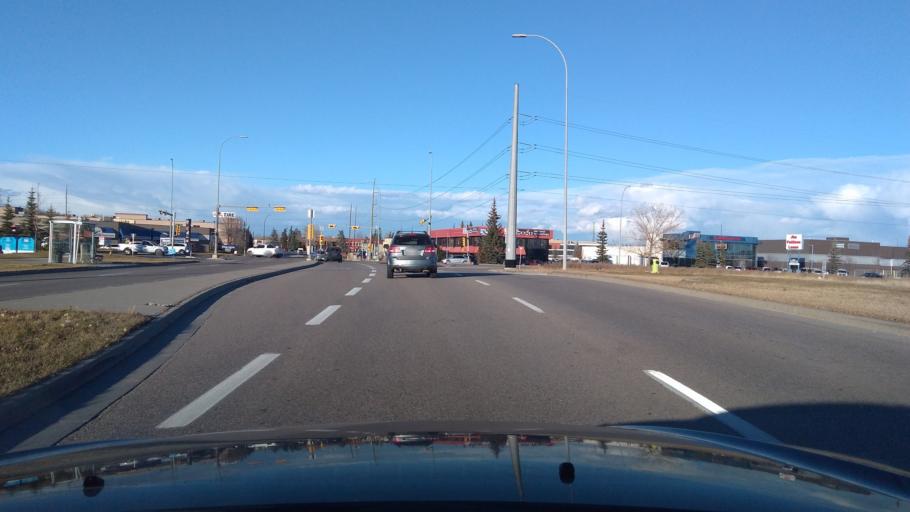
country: CA
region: Alberta
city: Calgary
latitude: 50.9862
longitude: -114.0398
